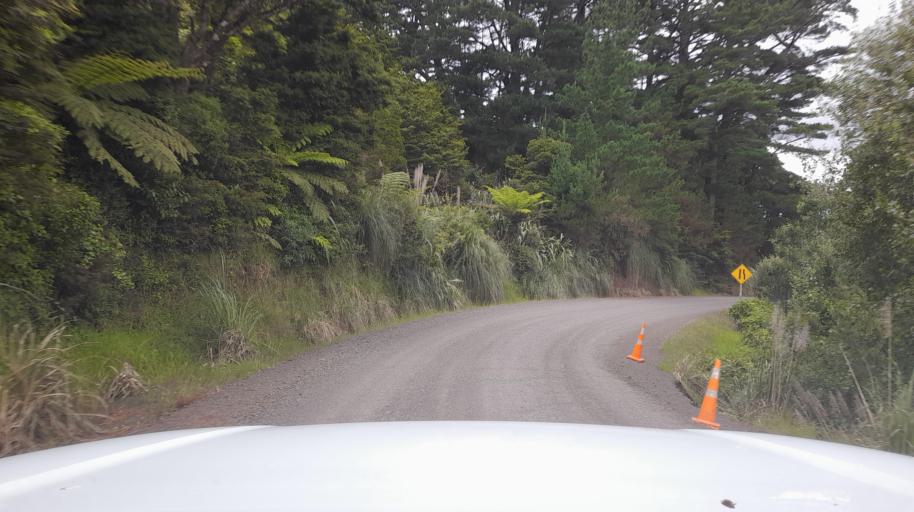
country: NZ
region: Northland
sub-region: Far North District
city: Kaitaia
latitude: -35.3284
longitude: 173.3531
